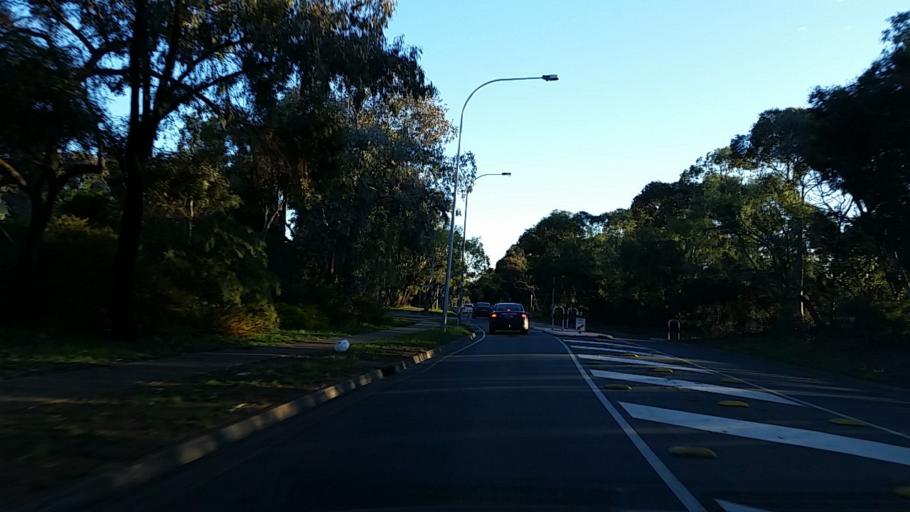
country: AU
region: South Australia
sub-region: Salisbury
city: Salisbury
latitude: -34.7778
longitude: 138.6120
